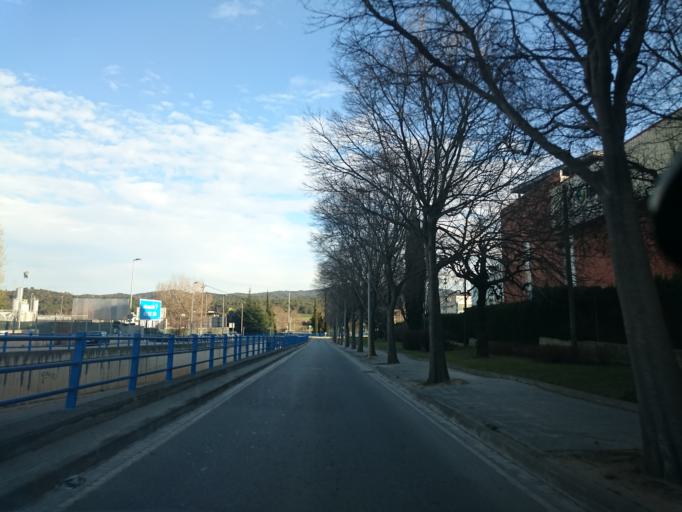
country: ES
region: Catalonia
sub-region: Provincia de Barcelona
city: Sant Cugat del Valles
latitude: 41.4783
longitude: 2.0950
